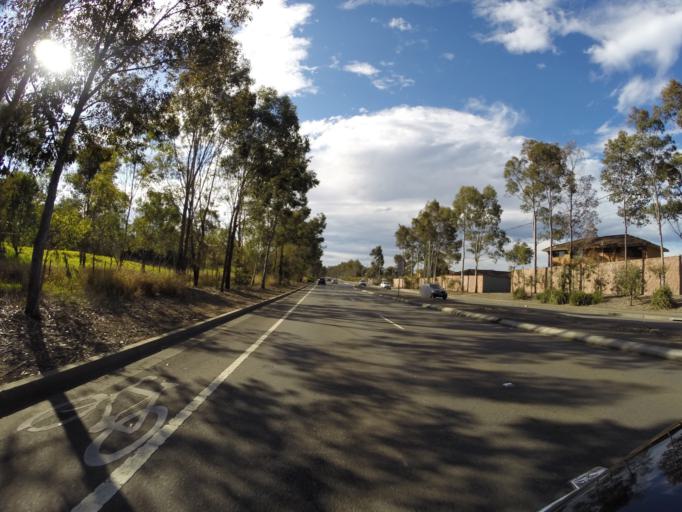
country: AU
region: New South Wales
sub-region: Fairfield
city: Horsley Park
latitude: -33.8592
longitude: 150.8731
